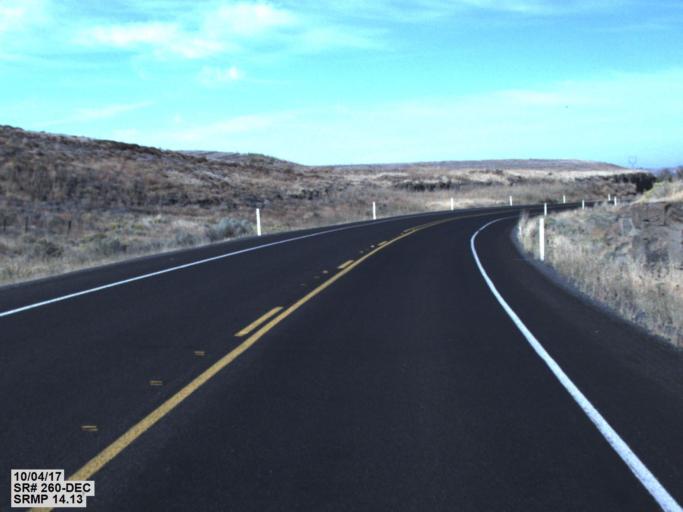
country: US
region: Washington
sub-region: Franklin County
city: Connell
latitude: 46.6319
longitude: -118.7549
